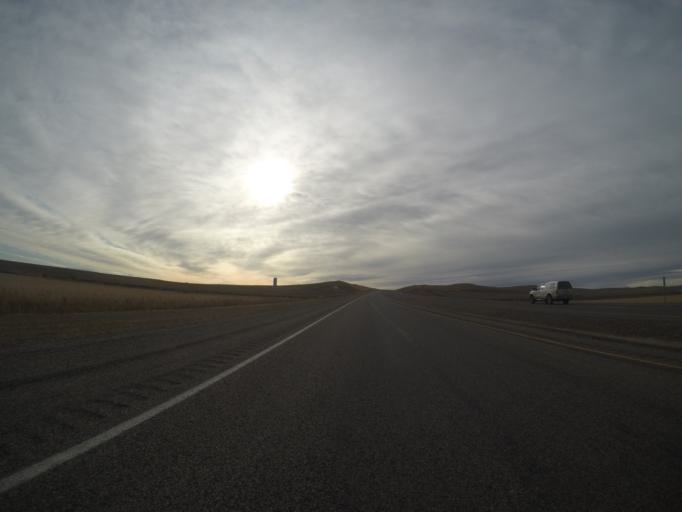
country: US
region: Montana
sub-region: Yellowstone County
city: Laurel
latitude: 45.6081
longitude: -108.8220
